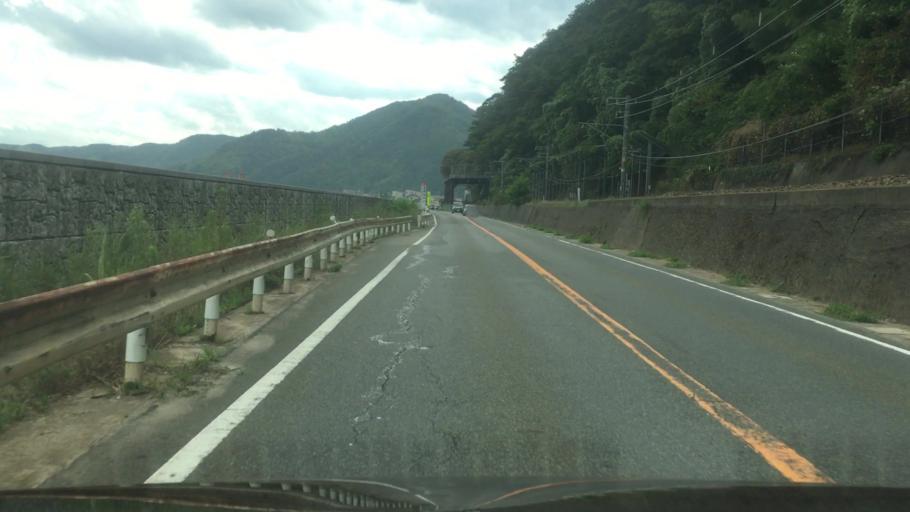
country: JP
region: Hyogo
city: Toyooka
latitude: 35.6130
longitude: 134.8071
